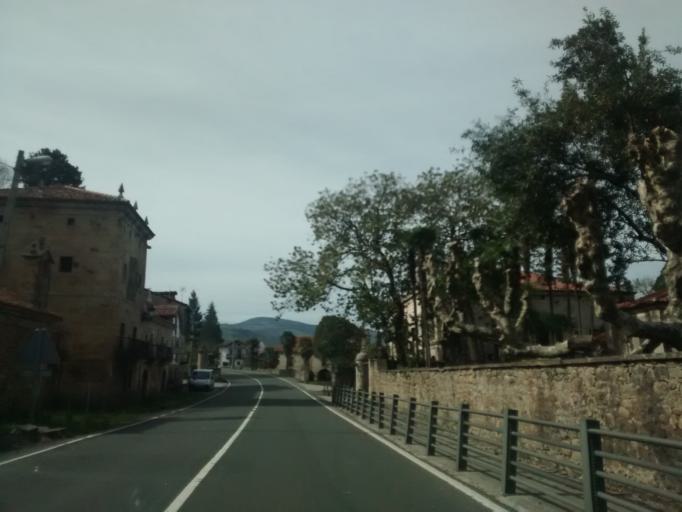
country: ES
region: Cantabria
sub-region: Provincia de Cantabria
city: Santiurde de Toranzo
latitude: 43.1929
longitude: -3.9163
